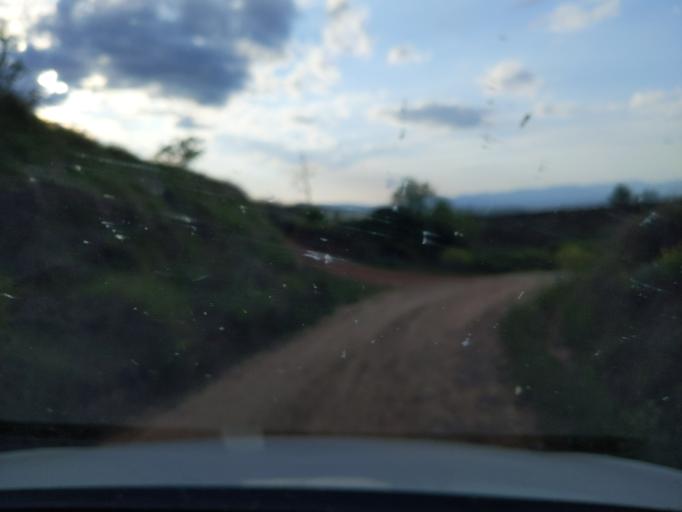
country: ES
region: La Rioja
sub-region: Provincia de La Rioja
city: Nalda
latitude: 42.3304
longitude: -2.4802
